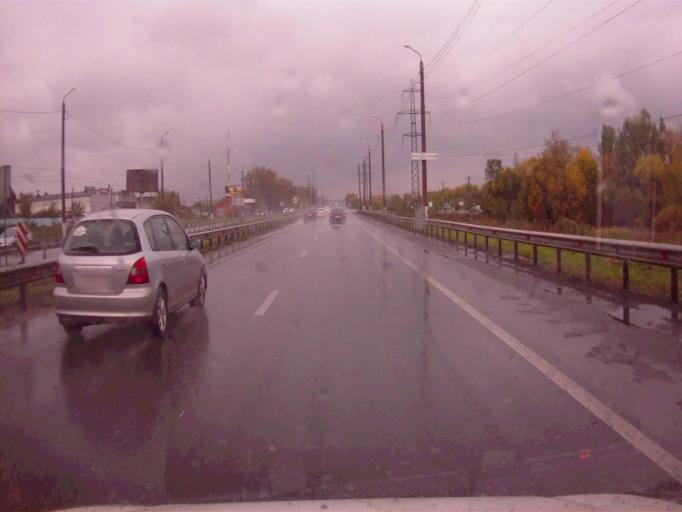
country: RU
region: Chelyabinsk
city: Dolgoderevenskoye
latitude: 55.2535
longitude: 61.3541
